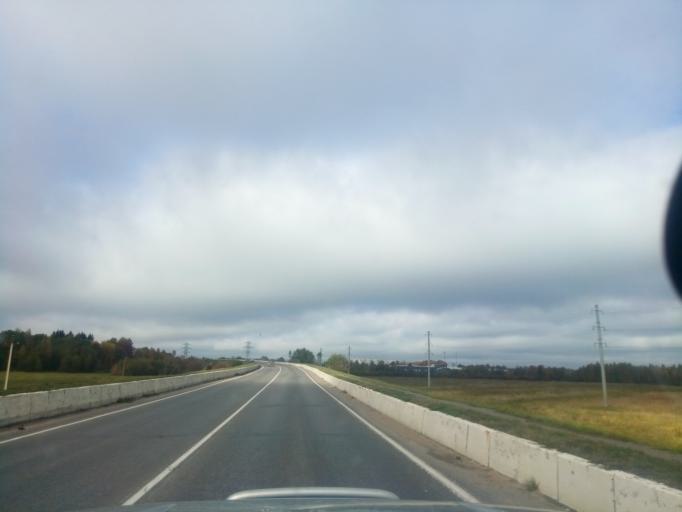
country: BY
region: Minsk
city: Zaslawye
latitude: 53.9970
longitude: 27.2892
